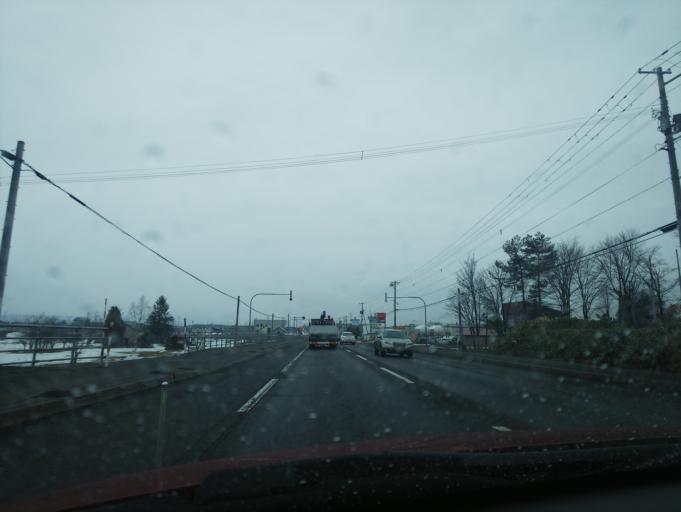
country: JP
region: Hokkaido
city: Nayoro
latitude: 44.1556
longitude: 142.3986
